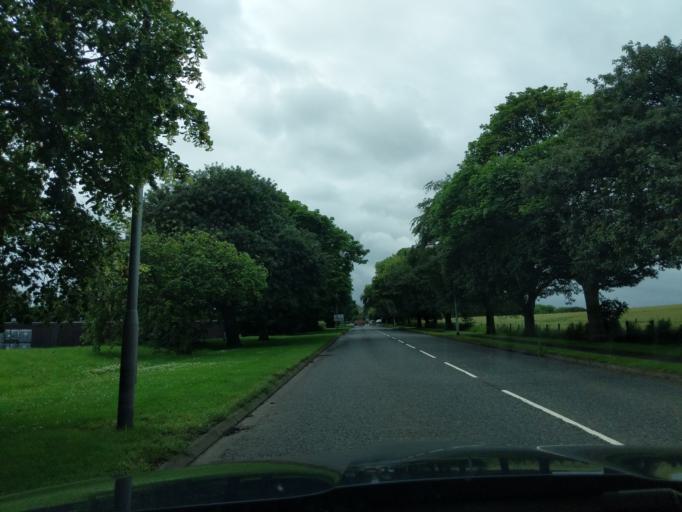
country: GB
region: England
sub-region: Northumberland
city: Berwick-Upon-Tweed
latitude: 55.7608
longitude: -2.0267
